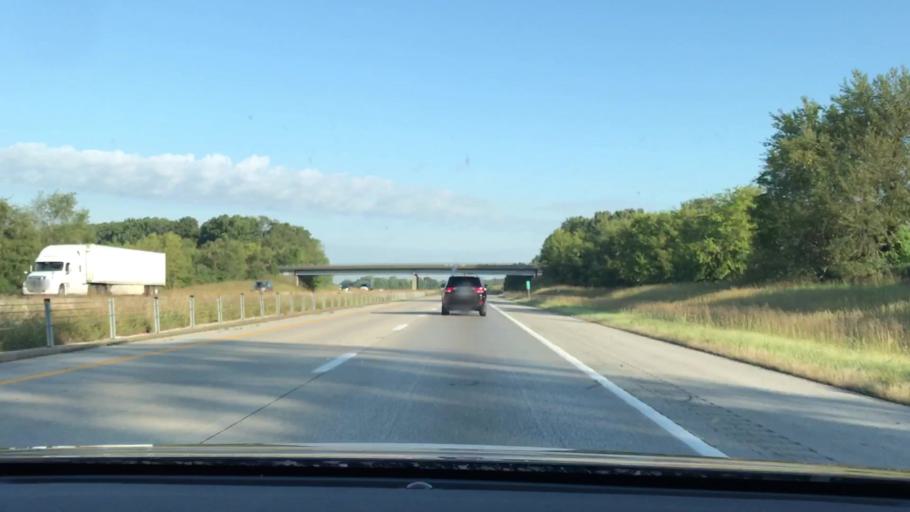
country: US
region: Kentucky
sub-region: Christian County
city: Oak Grove
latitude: 36.7264
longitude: -87.4880
